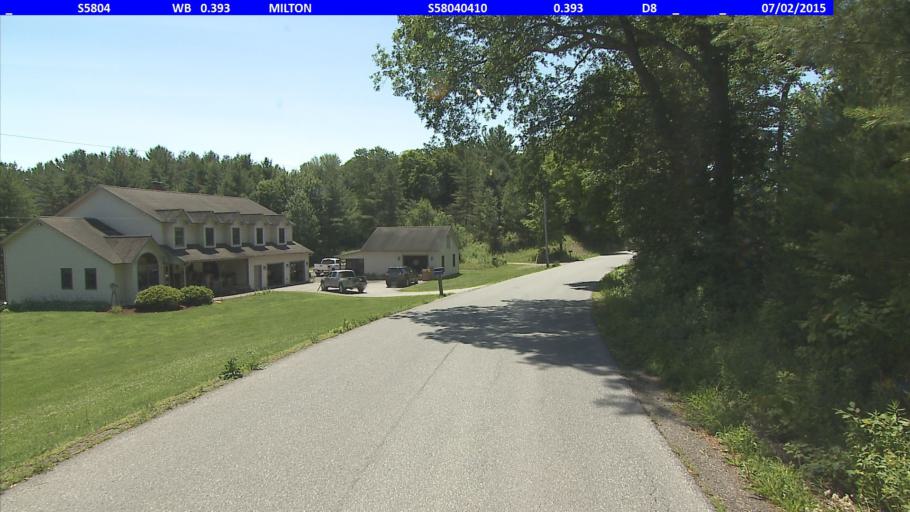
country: US
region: Vermont
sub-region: Chittenden County
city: Milton
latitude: 44.6525
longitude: -73.1633
